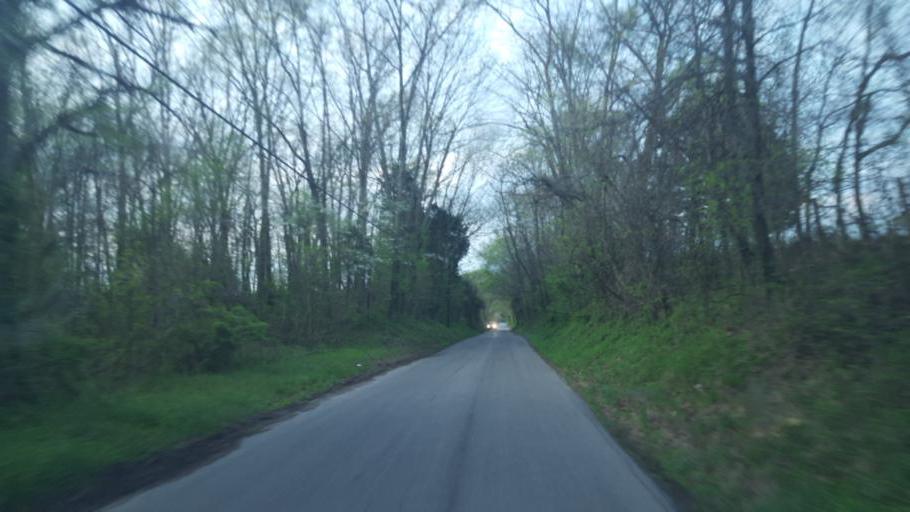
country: US
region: Kentucky
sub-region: Hart County
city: Munfordville
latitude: 37.2821
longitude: -85.9032
